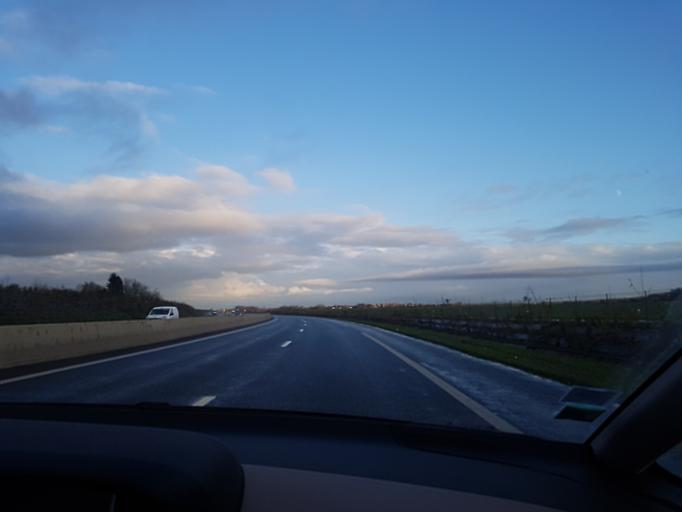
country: FR
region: Nord-Pas-de-Calais
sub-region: Departement du Pas-de-Calais
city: Houdain
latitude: 50.4511
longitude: 2.5530
